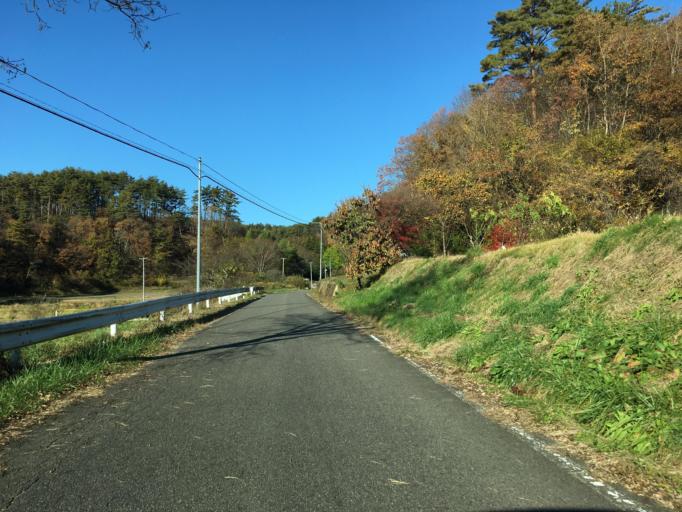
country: JP
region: Fukushima
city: Ishikawa
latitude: 37.2266
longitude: 140.5174
